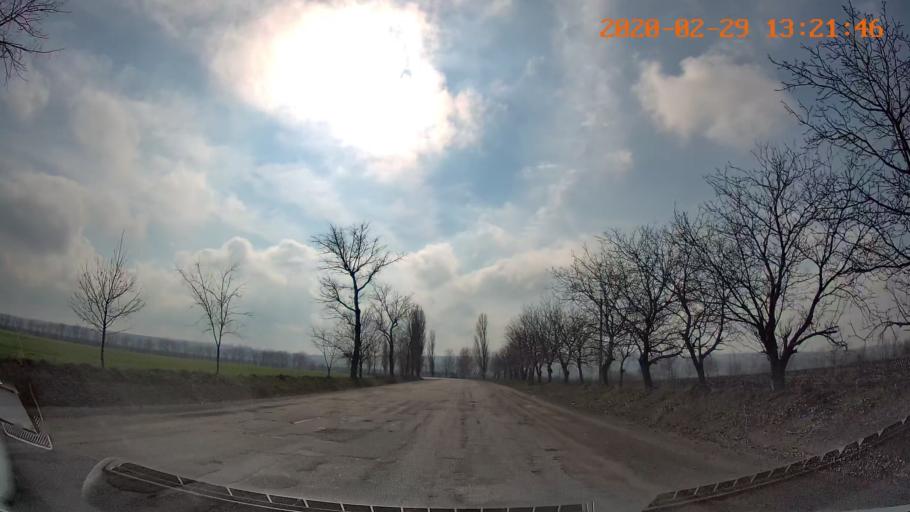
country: MD
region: Telenesti
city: Camenca
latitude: 47.9673
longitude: 28.6300
